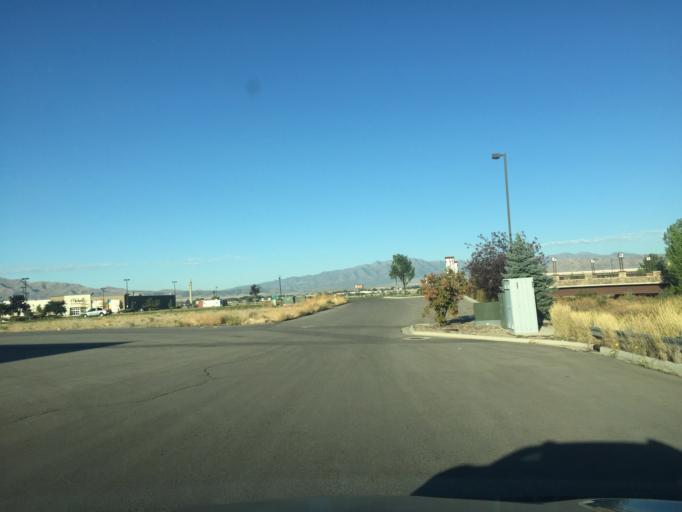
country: US
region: Utah
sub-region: Utah County
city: American Fork
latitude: 40.3833
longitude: -111.8182
